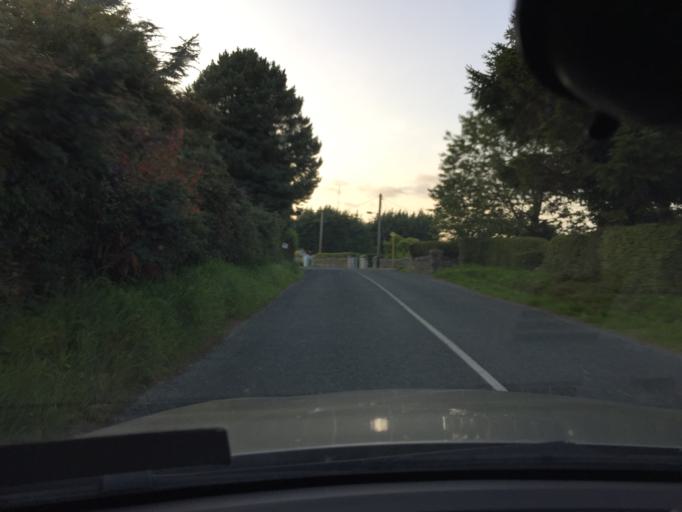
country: IE
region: Leinster
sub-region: Wicklow
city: Enniskerry
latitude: 53.1956
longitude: -6.1919
